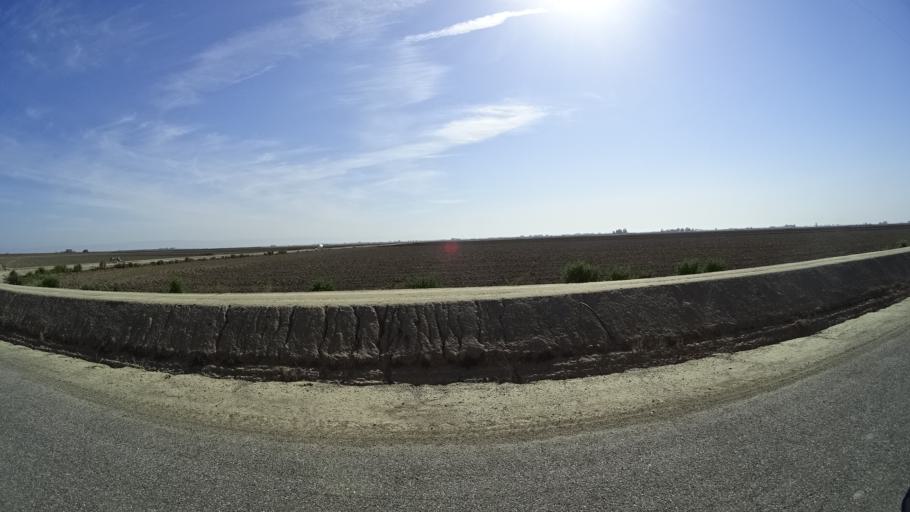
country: US
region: California
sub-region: Glenn County
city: Willows
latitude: 39.6103
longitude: -122.1171
